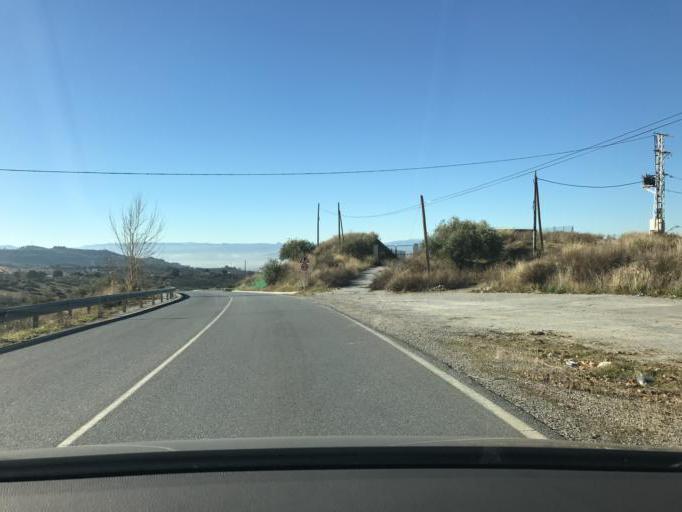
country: ES
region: Andalusia
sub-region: Provincia de Granada
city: Alfacar
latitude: 37.2309
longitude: -3.5725
